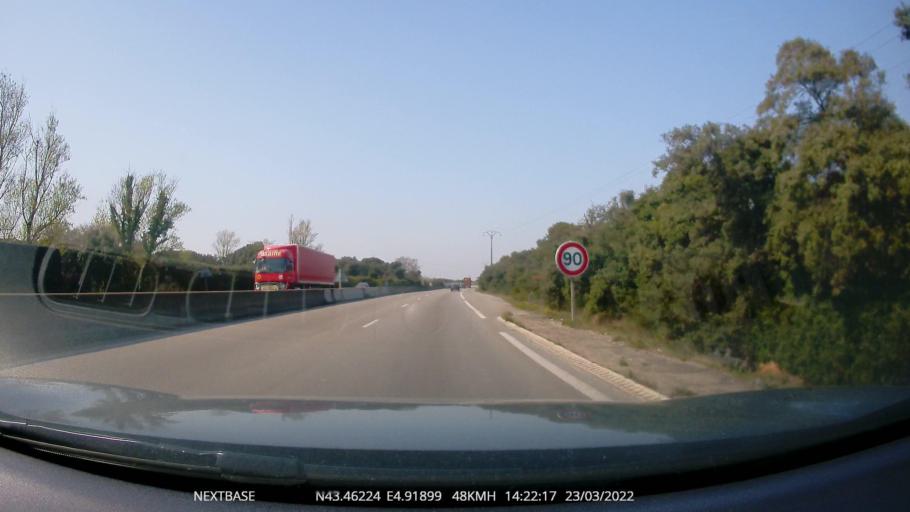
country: FR
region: Provence-Alpes-Cote d'Azur
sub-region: Departement des Bouches-du-Rhone
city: Fos-sur-Mer
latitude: 43.4700
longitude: 4.9103
